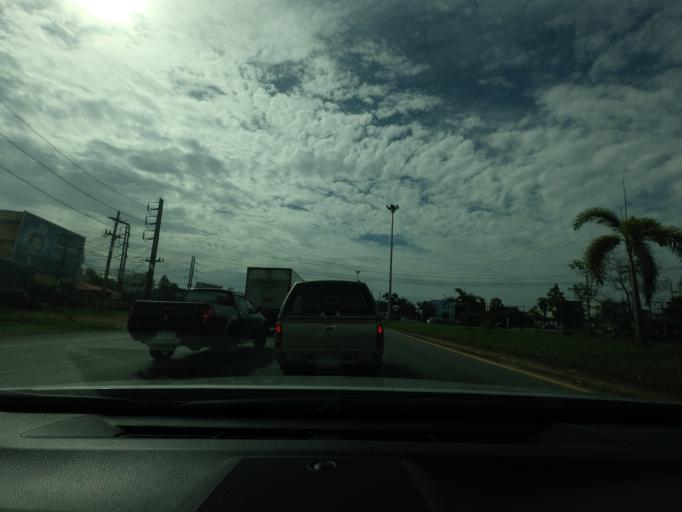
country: TH
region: Songkhla
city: Hat Yai
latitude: 6.9917
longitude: 100.4187
